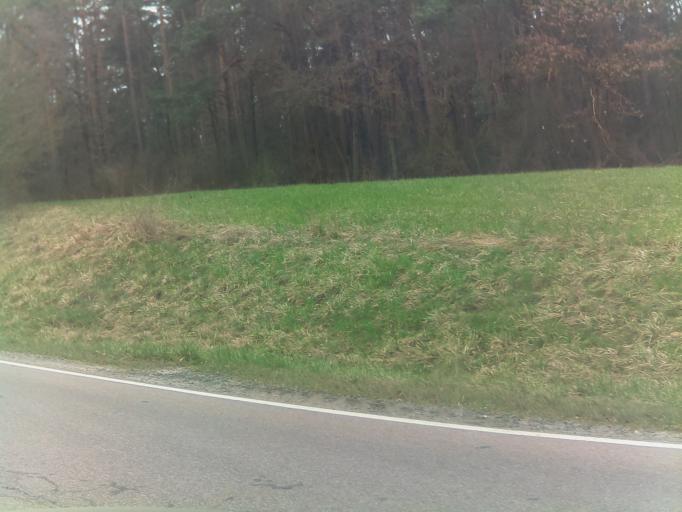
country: DE
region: Bavaria
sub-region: Upper Palatinate
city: Gebenbach
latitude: 49.4915
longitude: 11.8787
